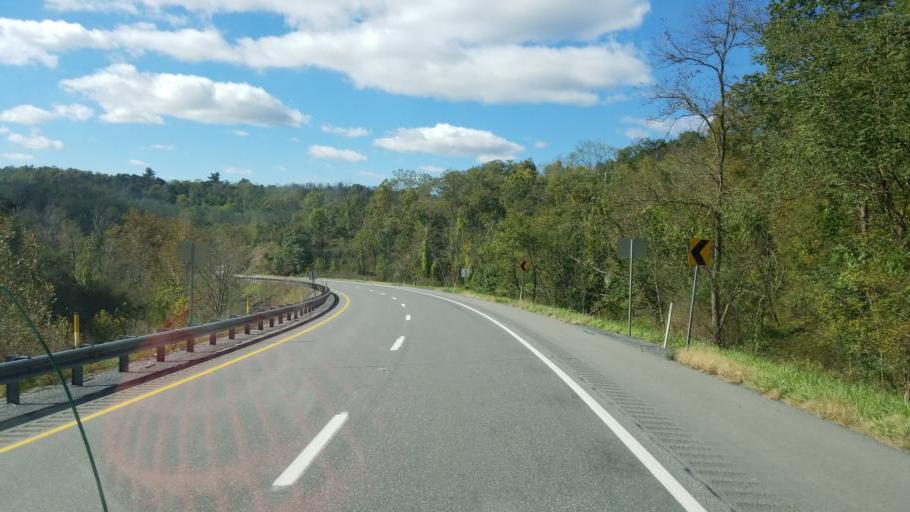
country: US
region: Pennsylvania
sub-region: Bedford County
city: Earlston
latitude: 39.9981
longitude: -78.2660
